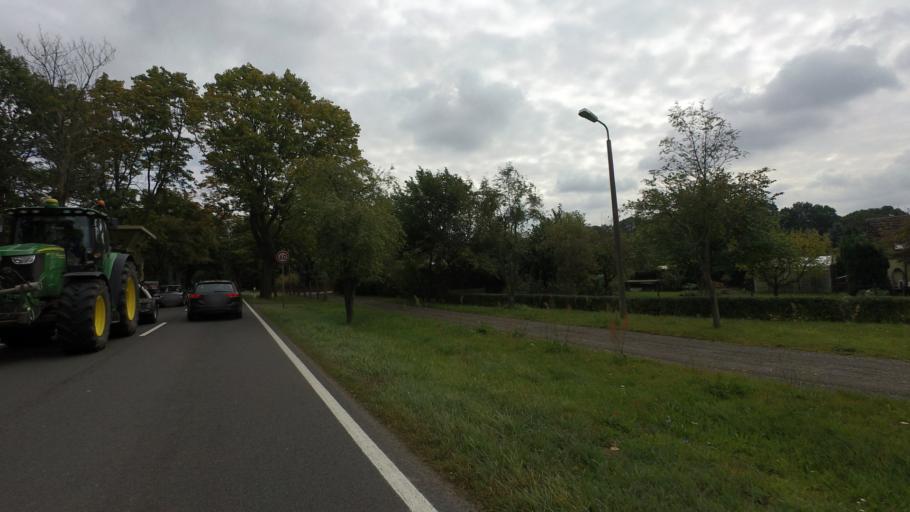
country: DE
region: Brandenburg
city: Golssen
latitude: 51.9760
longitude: 13.5946
